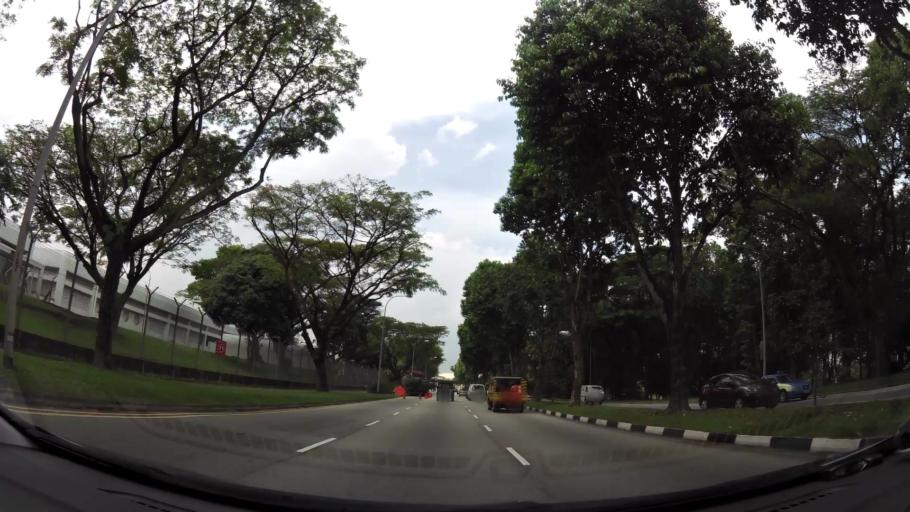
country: SG
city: Singapore
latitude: 1.3424
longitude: 103.9186
